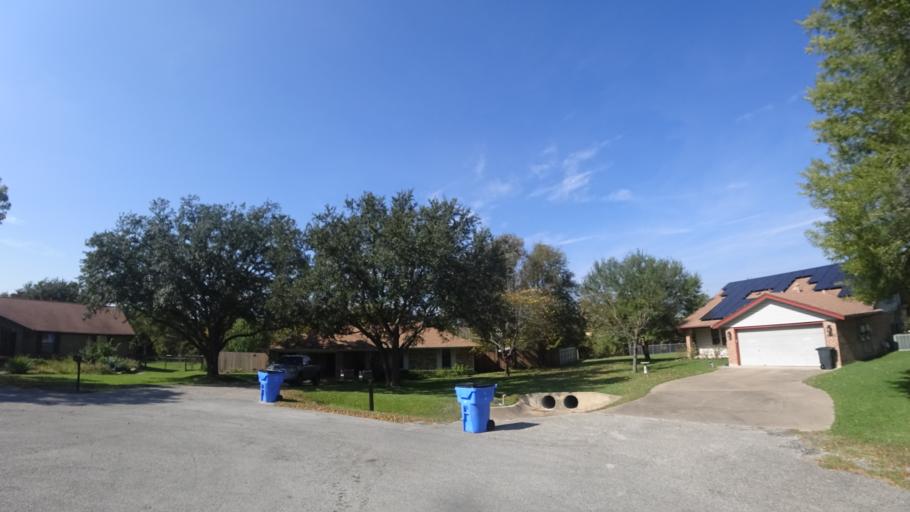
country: US
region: Texas
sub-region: Travis County
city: Pflugerville
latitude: 30.4195
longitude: -97.6276
